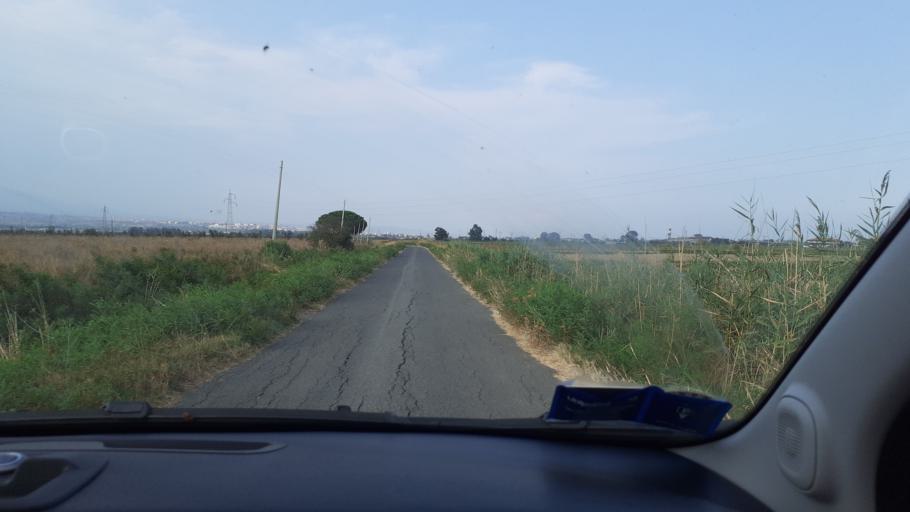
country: IT
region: Sicily
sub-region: Catania
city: Catania
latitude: 37.4270
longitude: 15.0115
